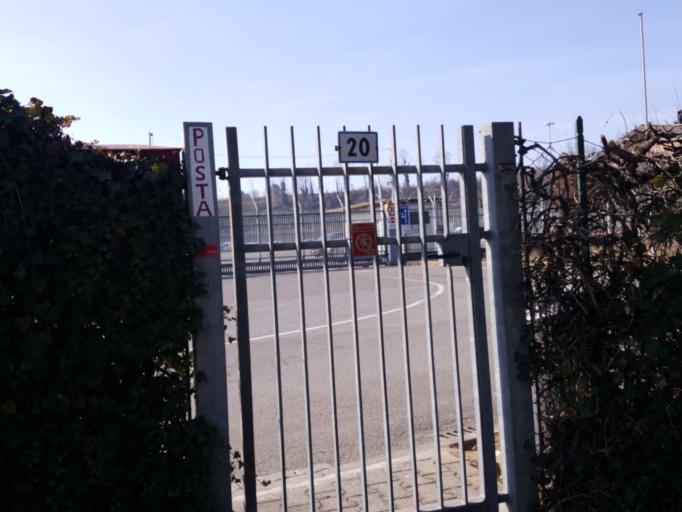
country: IT
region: Lombardy
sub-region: Provincia di Como
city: Carimate
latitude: 45.6957
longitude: 9.1093
